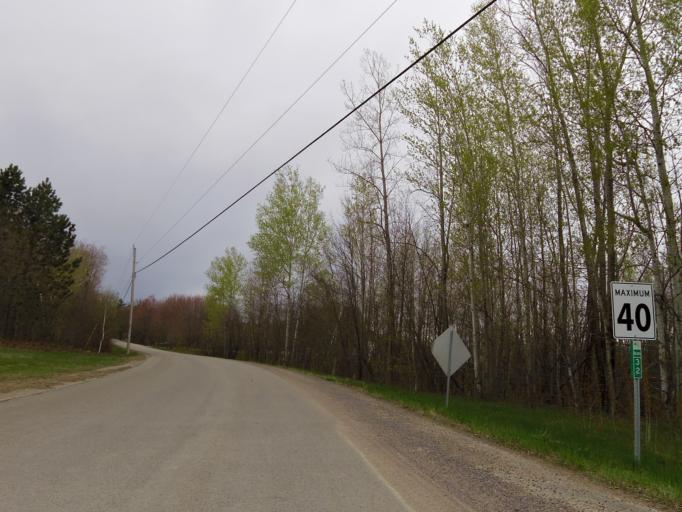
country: CA
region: Ontario
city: Hawkesbury
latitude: 45.6213
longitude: -74.5516
